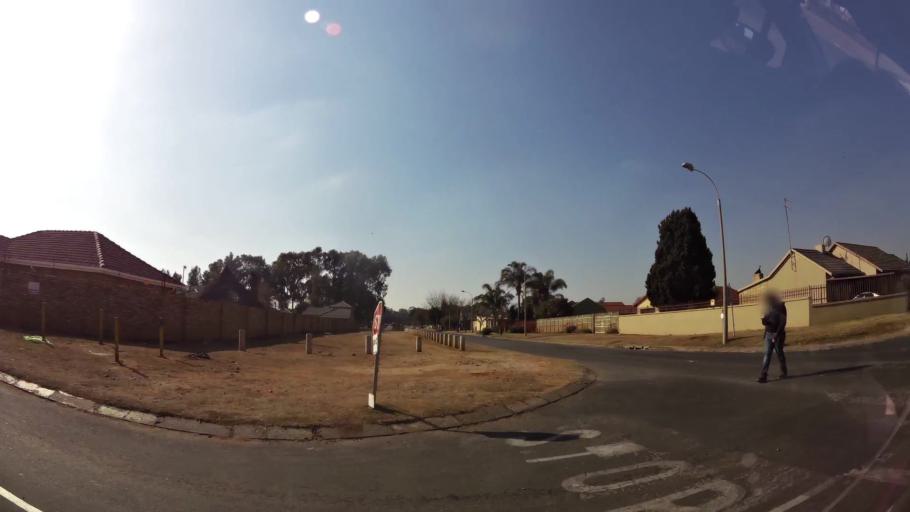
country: ZA
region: Gauteng
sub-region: West Rand District Municipality
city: Randfontein
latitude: -26.1787
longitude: 27.6925
